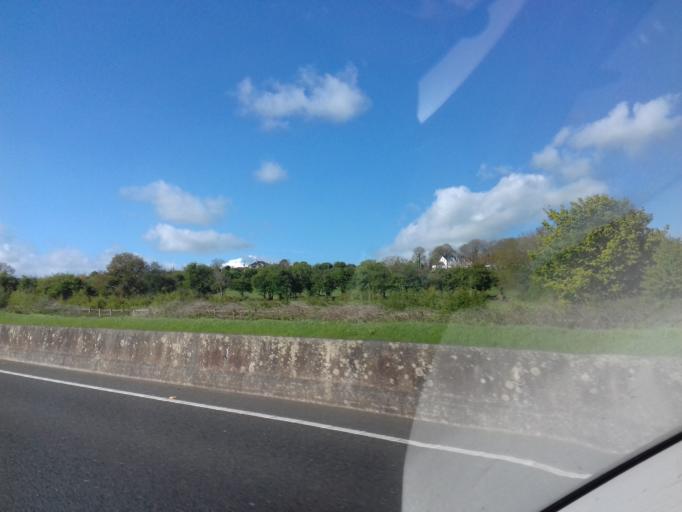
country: IE
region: Munster
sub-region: Waterford
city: Waterford
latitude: 52.3376
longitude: -7.1609
